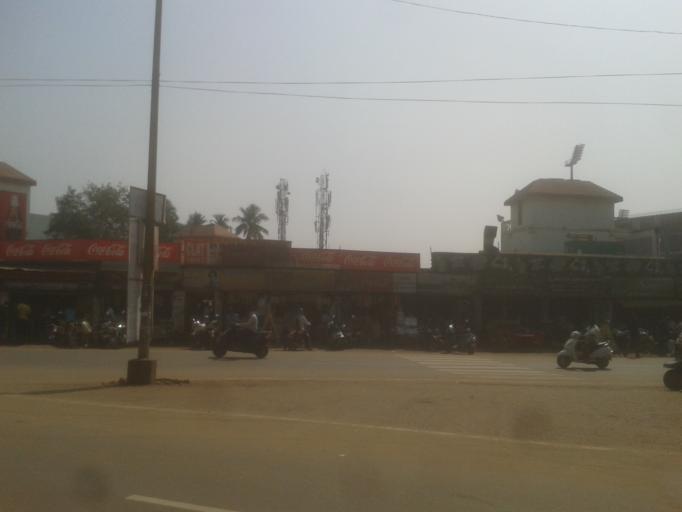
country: IN
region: Odisha
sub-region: Cuttack
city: Cuttack
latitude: 20.4836
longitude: 85.8667
